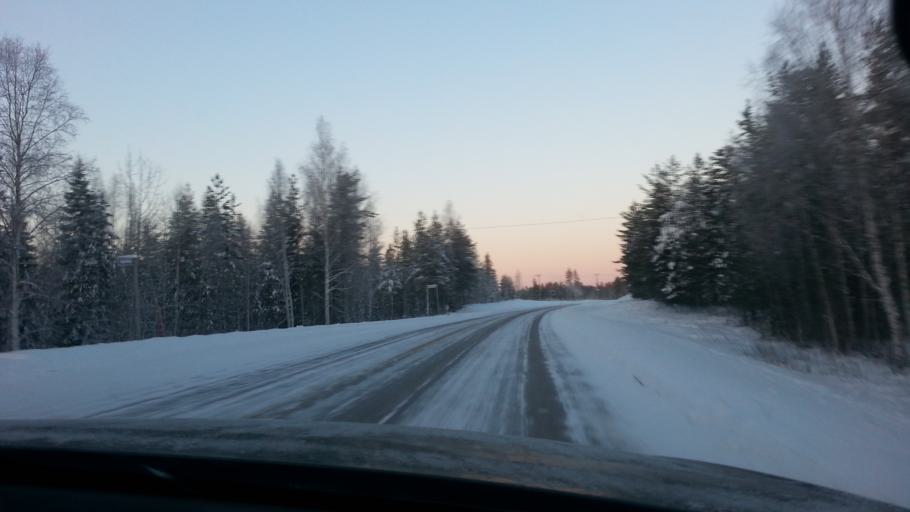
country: FI
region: Lapland
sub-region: Rovaniemi
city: Rovaniemi
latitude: 66.7812
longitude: 25.4460
